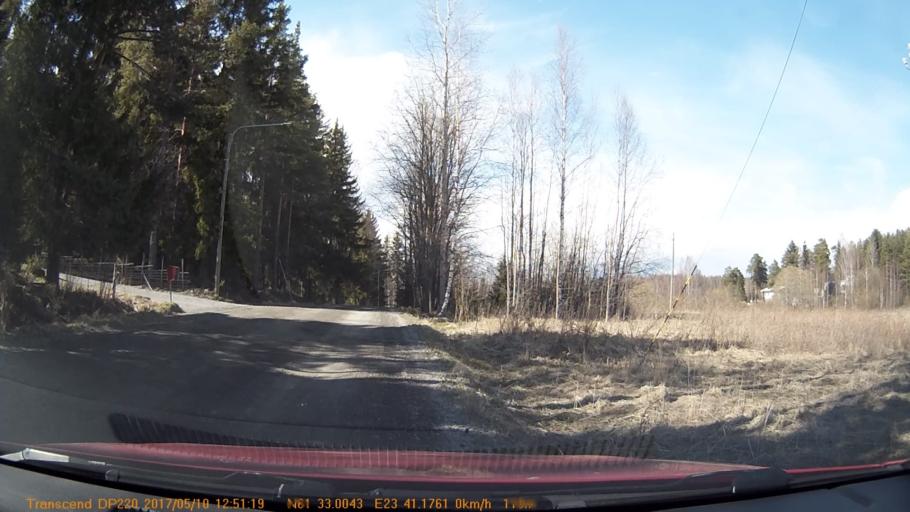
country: FI
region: Pirkanmaa
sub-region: Tampere
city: Yloejaervi
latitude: 61.5501
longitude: 23.6863
